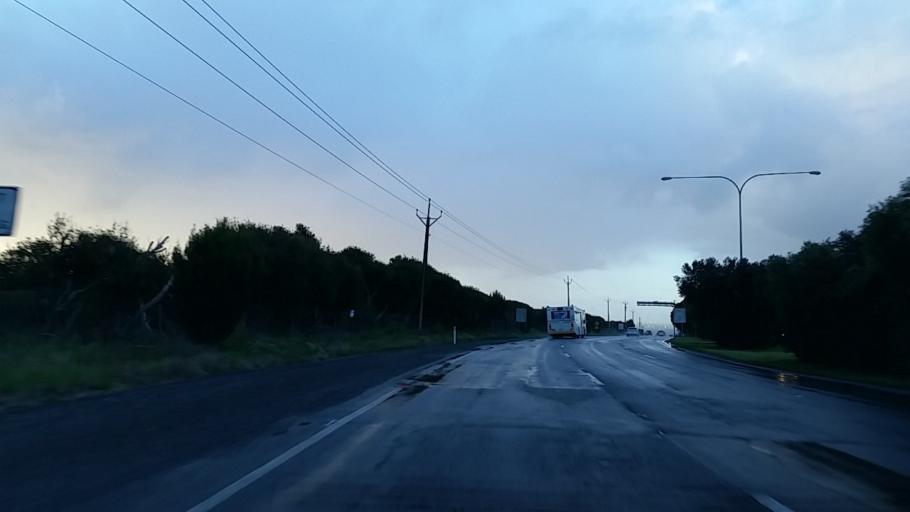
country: AU
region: South Australia
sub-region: Onkaparinga
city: Bedford Park
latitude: -35.0500
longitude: 138.5591
